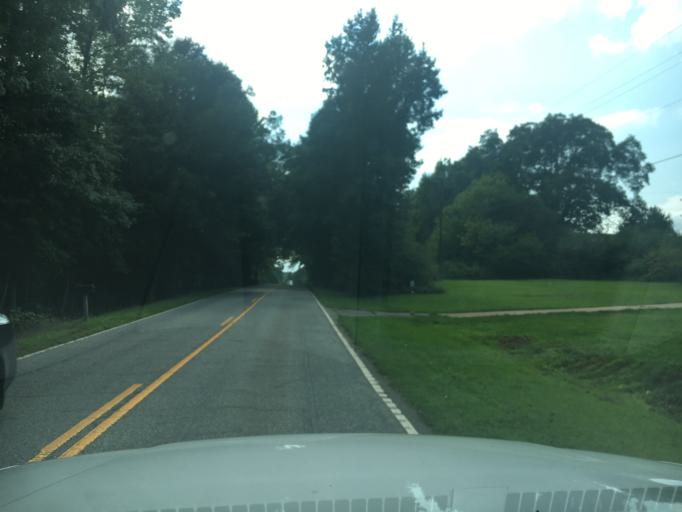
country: US
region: South Carolina
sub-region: Anderson County
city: Belton
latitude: 34.5351
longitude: -82.4603
